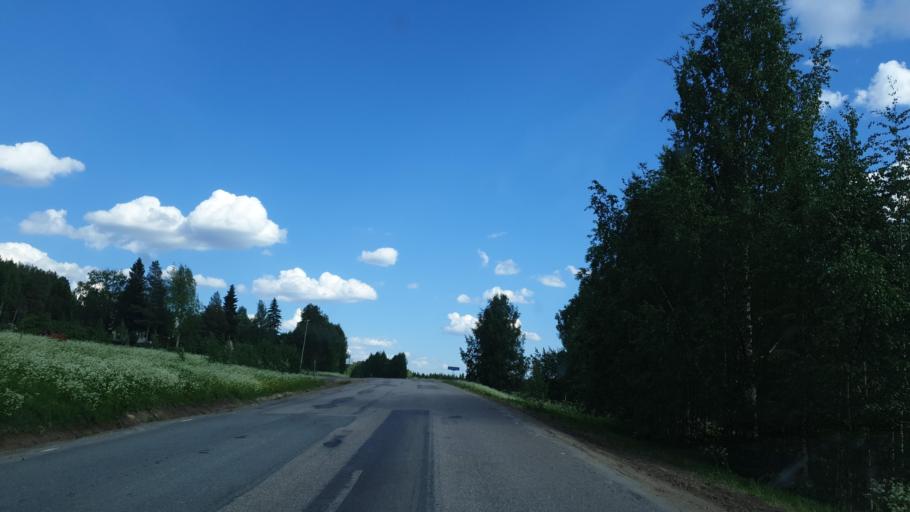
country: SE
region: Norrbotten
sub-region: Alvsbyns Kommun
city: AElvsbyn
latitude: 65.8544
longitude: 20.4347
